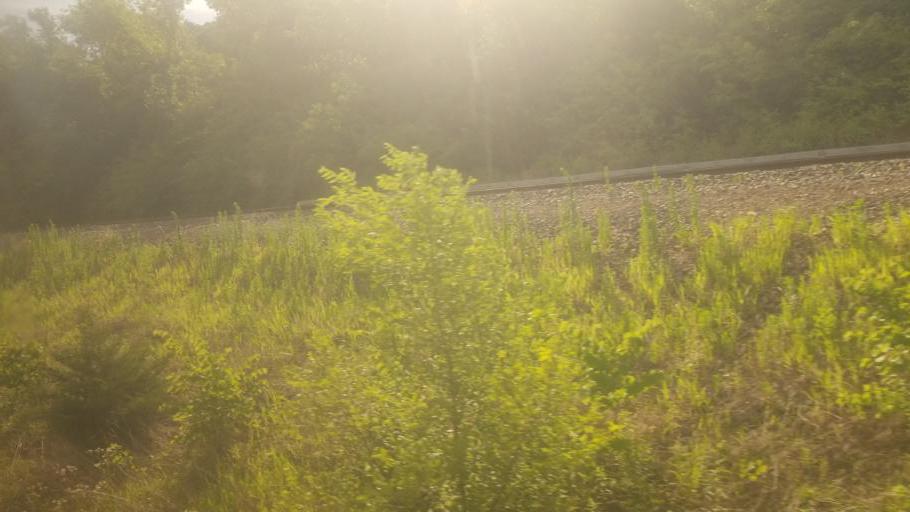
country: US
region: Kansas
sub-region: Johnson County
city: Shawnee
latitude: 39.0785
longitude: -94.7248
